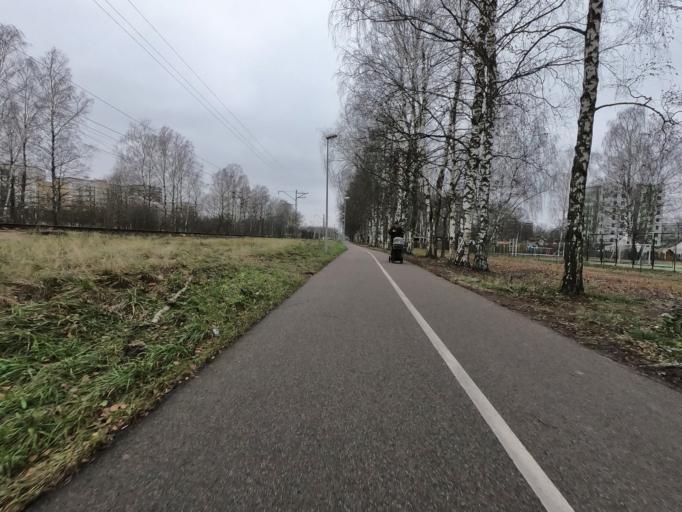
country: LV
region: Marupe
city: Marupe
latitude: 56.9504
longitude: 24.0066
